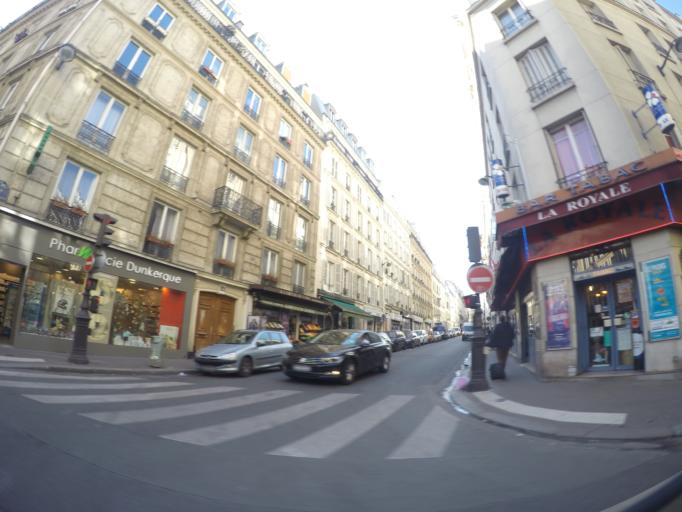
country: FR
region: Ile-de-France
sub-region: Paris
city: Saint-Ouen
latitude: 48.8811
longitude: 2.3498
